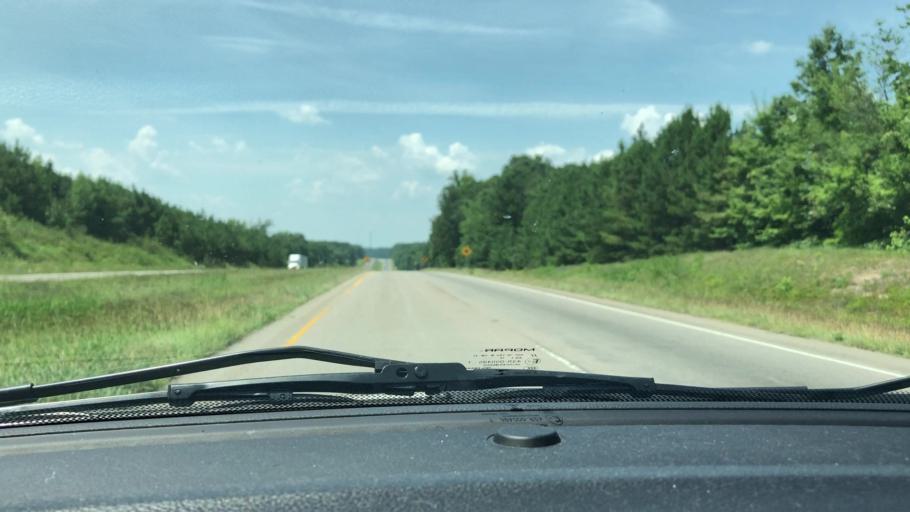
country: US
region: North Carolina
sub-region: Chatham County
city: Siler City
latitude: 35.6282
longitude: -79.3654
